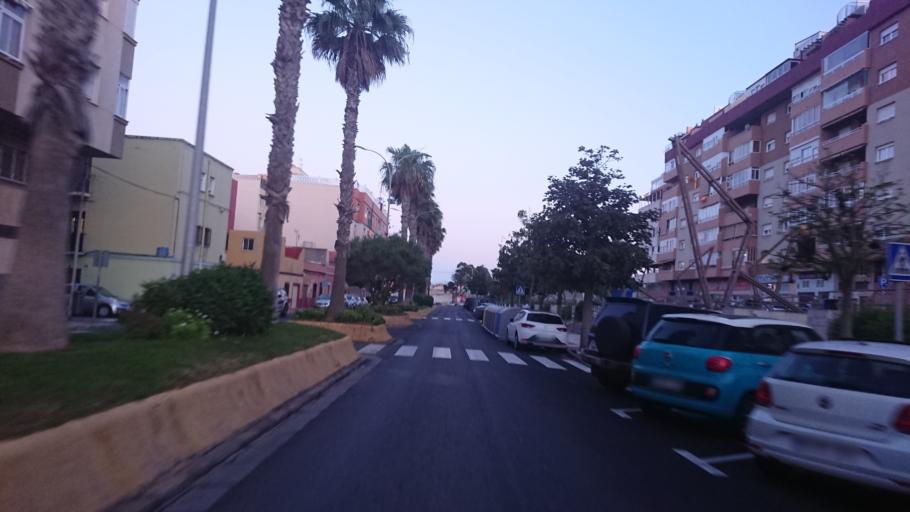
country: ES
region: Melilla
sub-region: Melilla
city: Melilla
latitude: 35.2740
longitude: -2.9471
